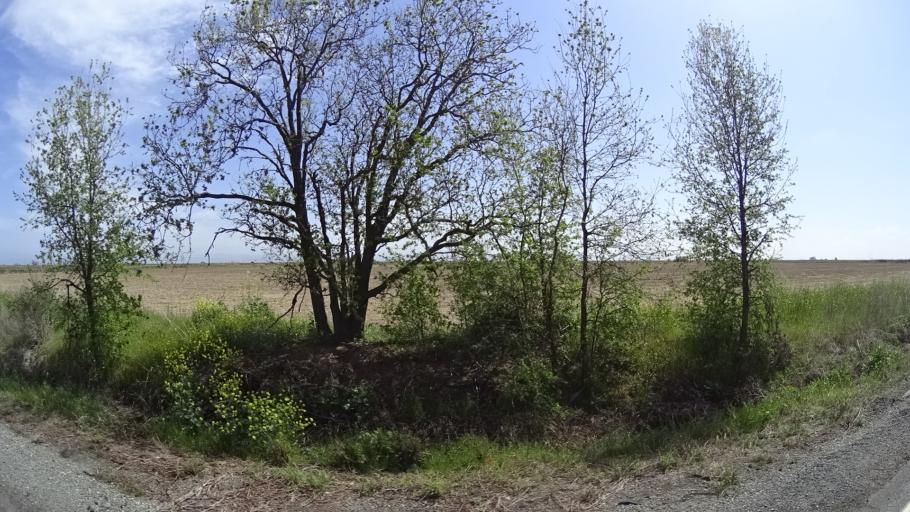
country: US
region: California
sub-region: Butte County
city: Durham
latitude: 39.4917
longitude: -121.8575
